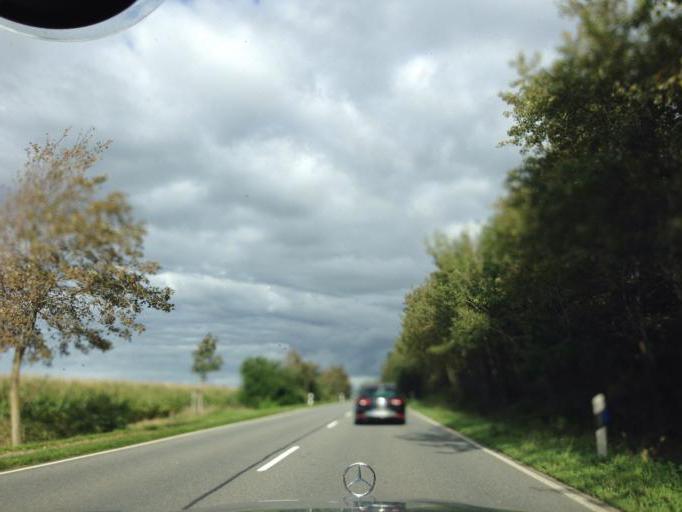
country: DE
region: Schleswig-Holstein
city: Leck
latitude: 54.7432
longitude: 8.9588
